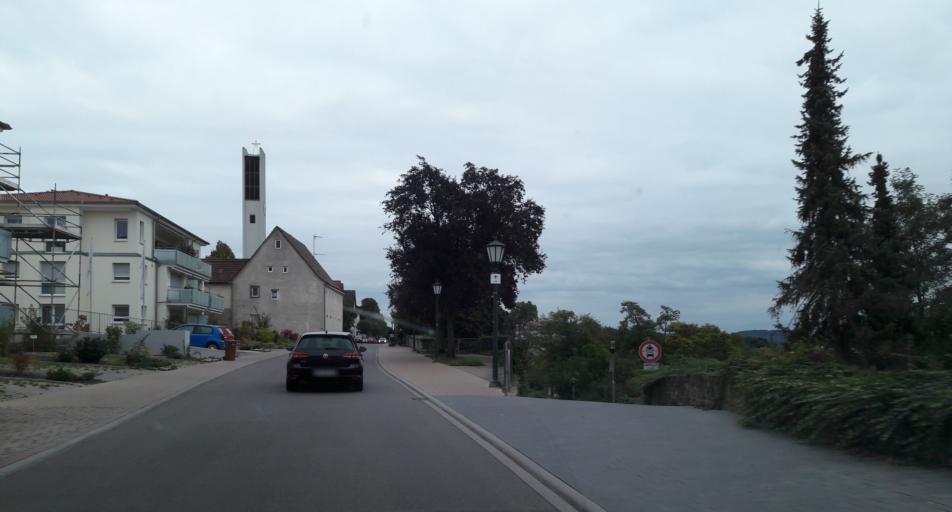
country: DE
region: Baden-Wuerttemberg
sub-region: Regierungsbezirk Stuttgart
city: Untereisesheim
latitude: 49.2336
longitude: 9.1891
